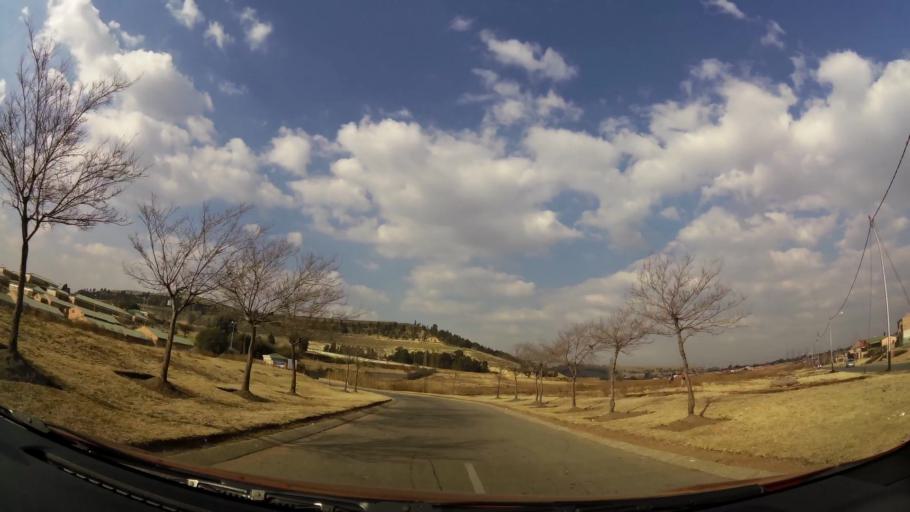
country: ZA
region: Gauteng
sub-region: City of Johannesburg Metropolitan Municipality
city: Soweto
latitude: -26.2282
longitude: 27.9412
